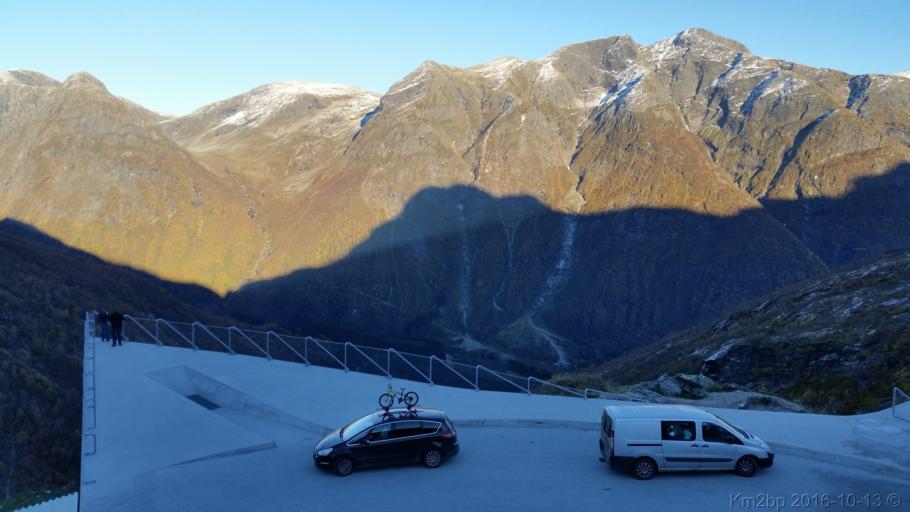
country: NO
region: Sogn og Fjordane
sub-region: Balestrand
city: Balestrand
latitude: 61.3515
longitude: 6.5184
